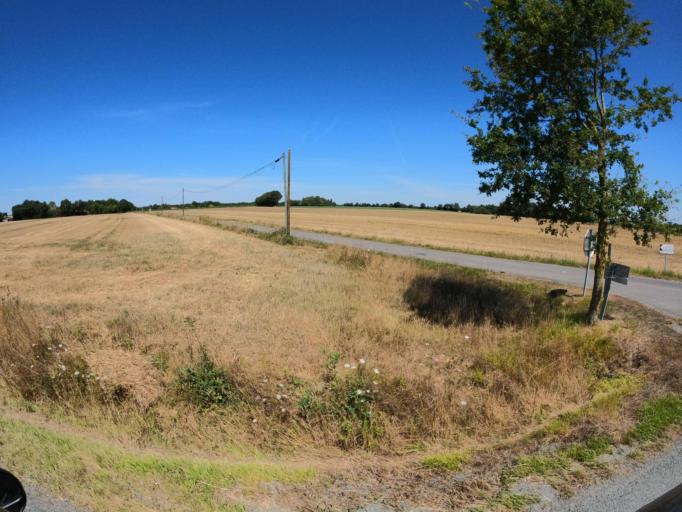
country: FR
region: Pays de la Loire
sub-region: Departement de la Vendee
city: Saint-Philbert-de-Bouaine
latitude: 46.9764
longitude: -1.5457
